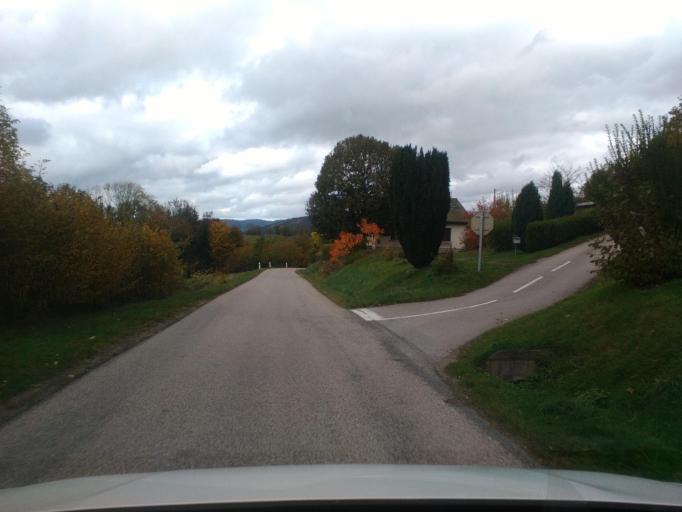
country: FR
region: Lorraine
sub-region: Departement des Vosges
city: Senones
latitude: 48.3411
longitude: 7.0239
